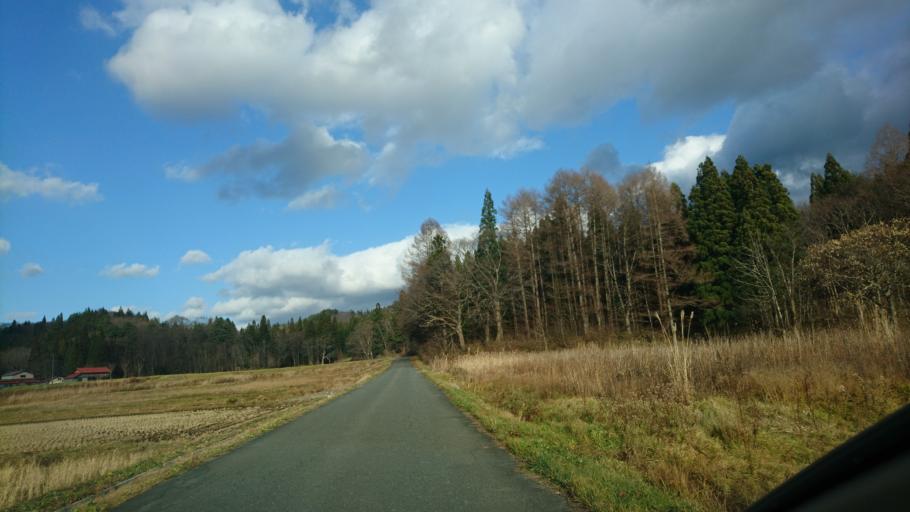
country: JP
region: Akita
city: Kakunodatemachi
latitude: 39.4617
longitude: 140.7869
